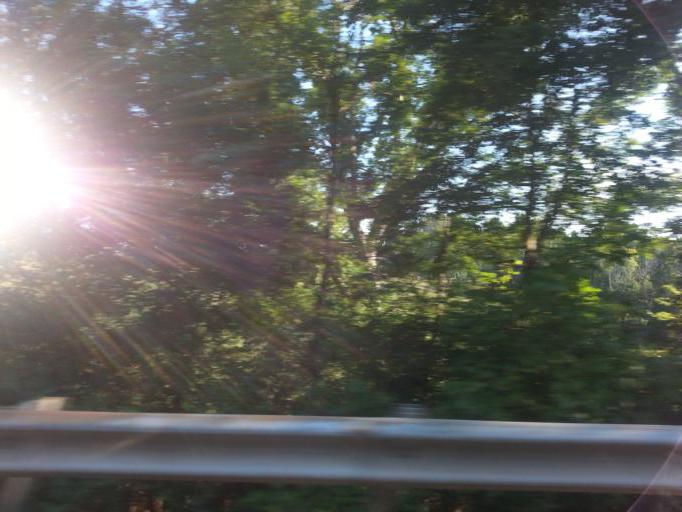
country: US
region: Tennessee
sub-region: Knox County
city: Knoxville
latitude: 35.8893
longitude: -83.9292
